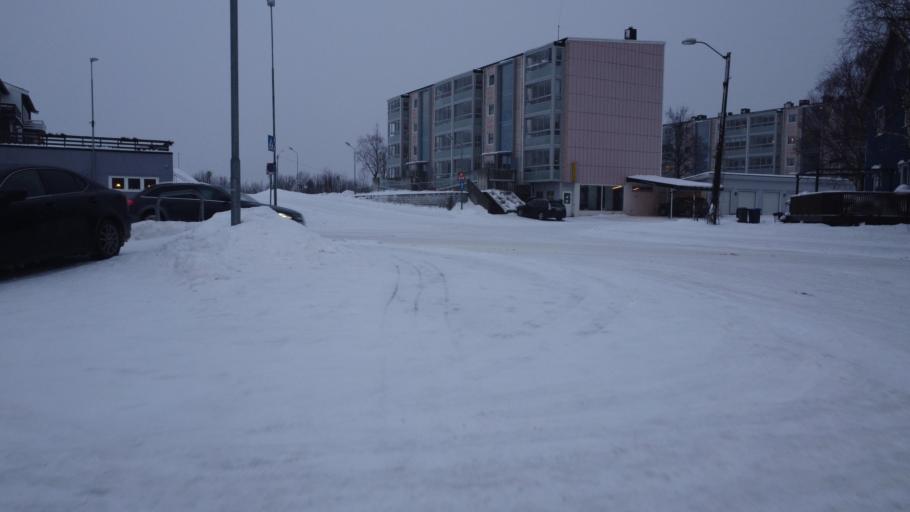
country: NO
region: Nordland
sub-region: Rana
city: Mo i Rana
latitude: 66.3178
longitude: 14.1594
